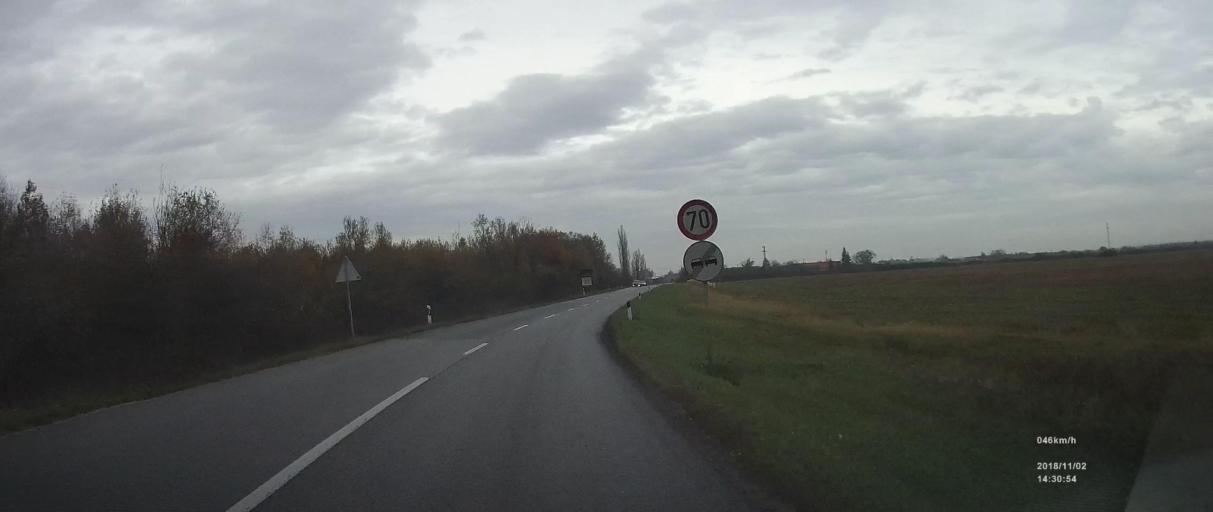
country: HR
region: Zagrebacka
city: Gradici
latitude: 45.6813
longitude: 16.0559
